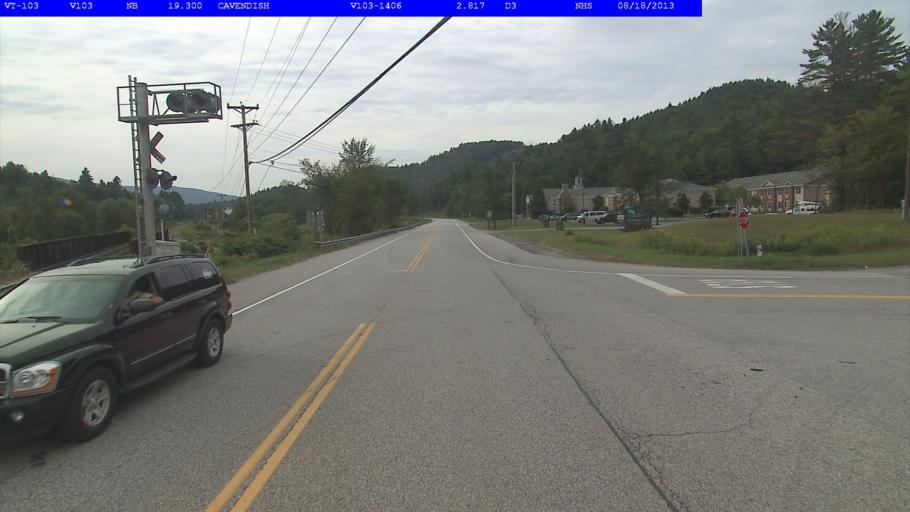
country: US
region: Vermont
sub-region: Windsor County
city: Chester
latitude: 43.3825
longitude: -72.6468
